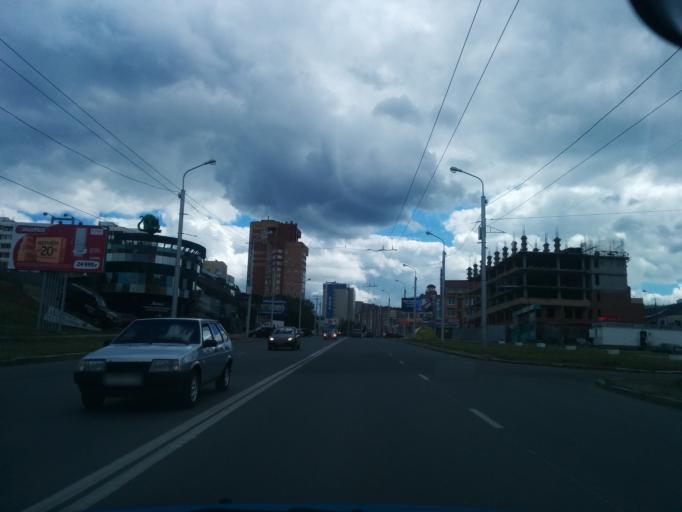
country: RU
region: Bashkortostan
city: Ufa
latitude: 54.7174
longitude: 55.9923
